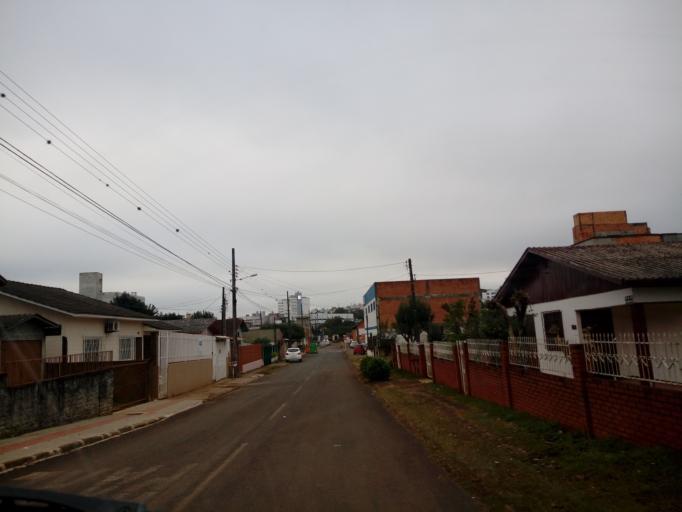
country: BR
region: Santa Catarina
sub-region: Chapeco
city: Chapeco
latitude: -27.0870
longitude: -52.6254
